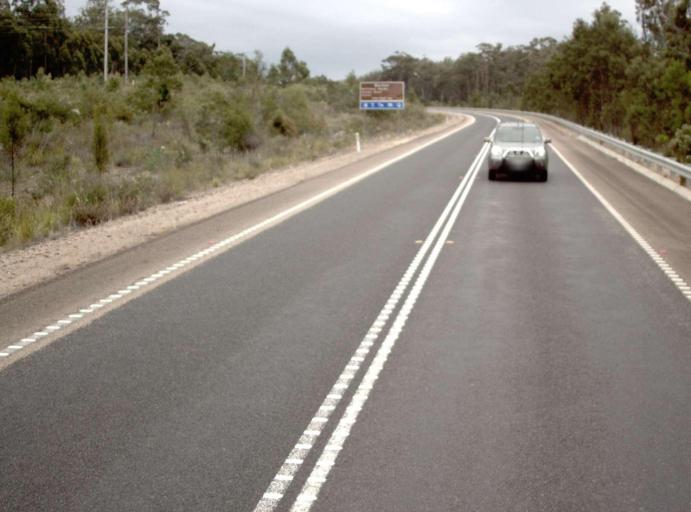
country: AU
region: Victoria
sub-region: East Gippsland
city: Lakes Entrance
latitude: -37.6997
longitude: 148.0497
